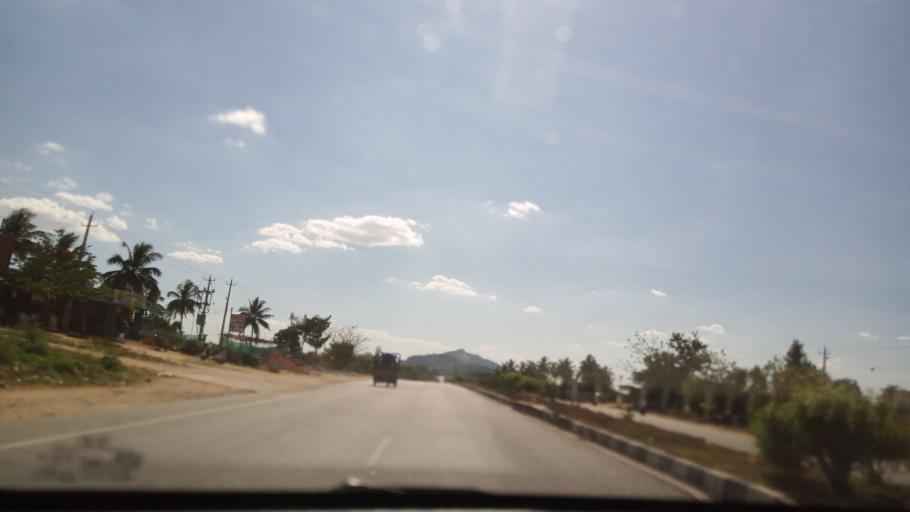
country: IN
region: Karnataka
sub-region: Kolar
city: Mulbagal
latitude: 13.1911
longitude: 78.4375
